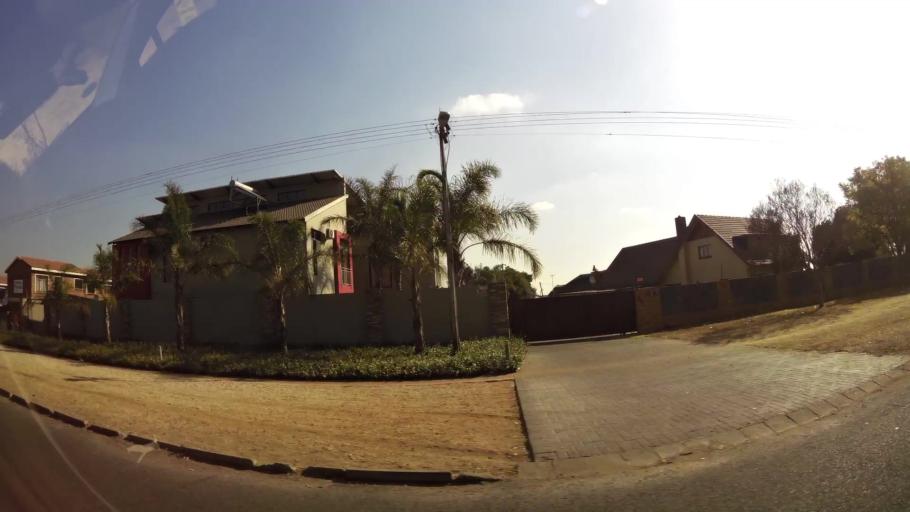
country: ZA
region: Gauteng
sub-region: West Rand District Municipality
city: Randfontein
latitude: -26.1631
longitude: 27.6988
